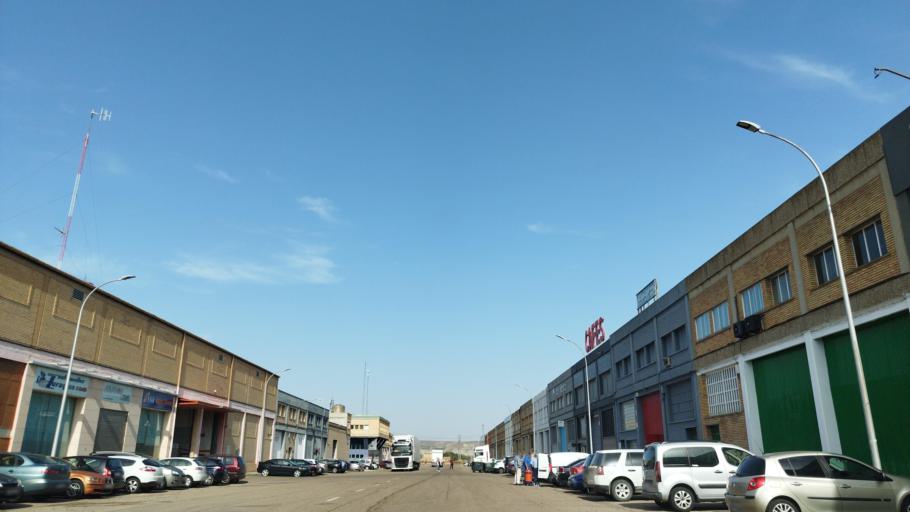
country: ES
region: Aragon
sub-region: Provincia de Zaragoza
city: Oliver-Valdefierro, Oliver, Valdefierro
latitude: 41.6719
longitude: -0.9471
